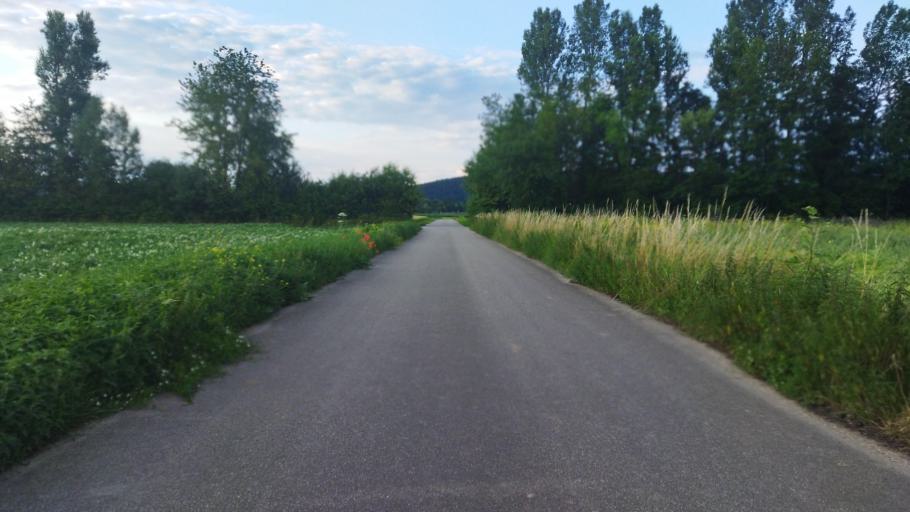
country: DE
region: Bavaria
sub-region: Upper Palatinate
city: Pfatter
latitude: 48.9888
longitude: 12.3805
